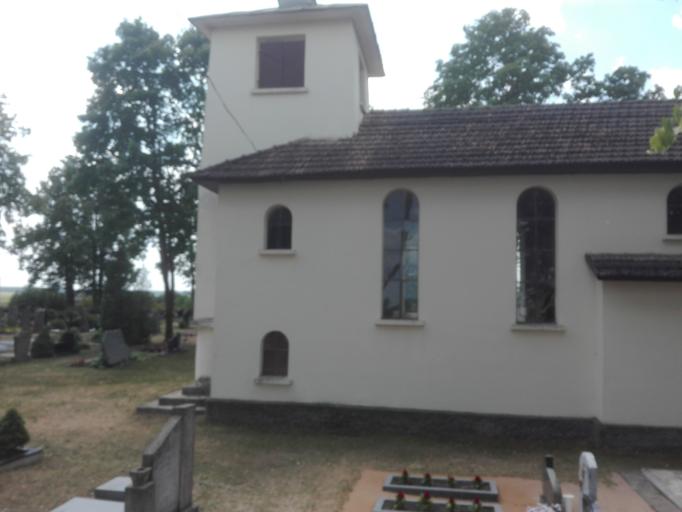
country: LT
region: Panevezys
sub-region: Birzai
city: Birzai
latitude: 56.1159
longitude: 24.8847
